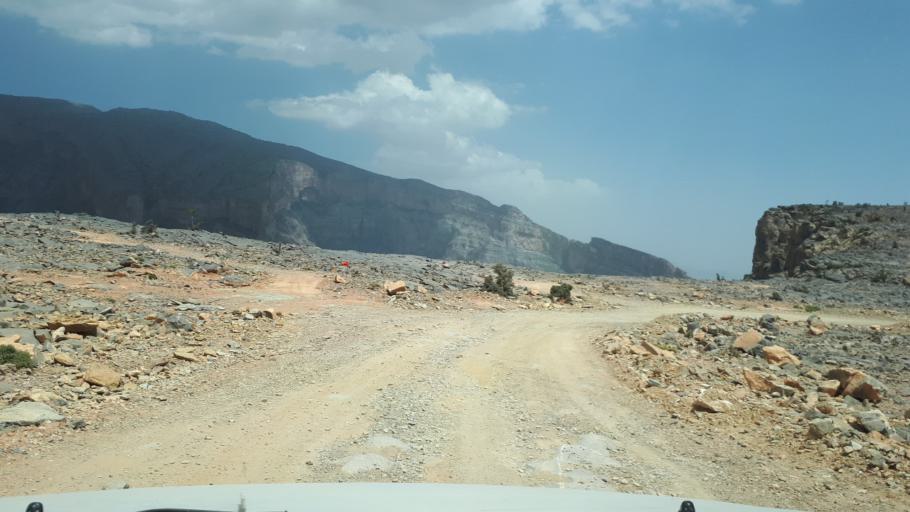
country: OM
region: Muhafazat ad Dakhiliyah
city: Bahla'
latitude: 23.2009
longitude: 57.2008
